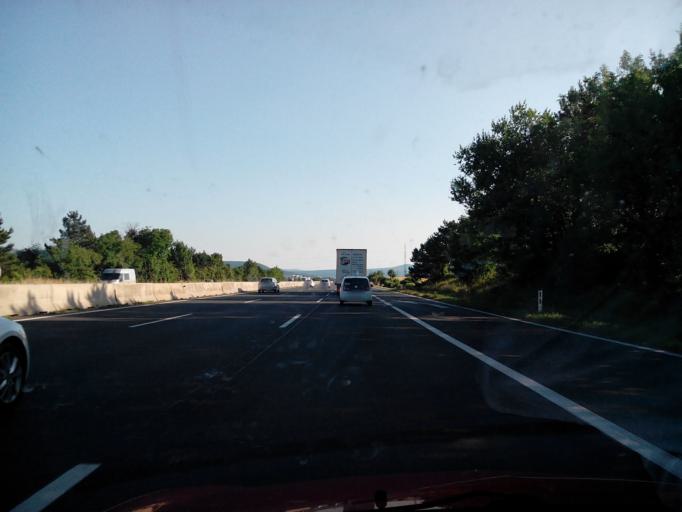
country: AT
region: Lower Austria
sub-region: Politischer Bezirk Baden
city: Leobersdorf
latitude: 47.9116
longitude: 16.2082
